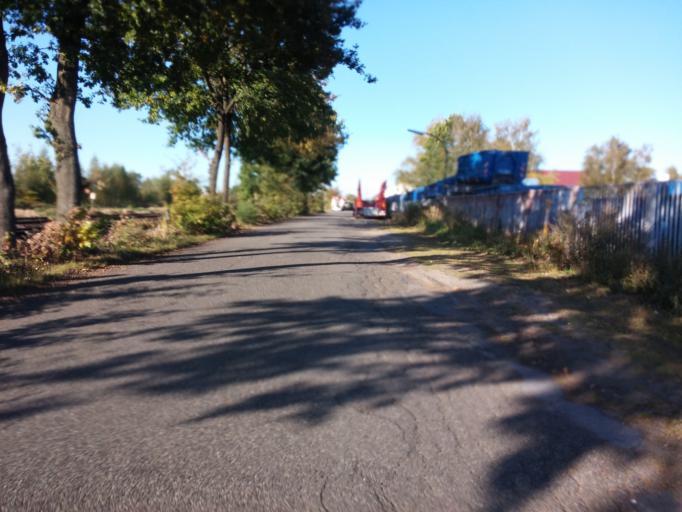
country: DE
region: North Rhine-Westphalia
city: Dorsten
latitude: 51.6529
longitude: 6.9714
